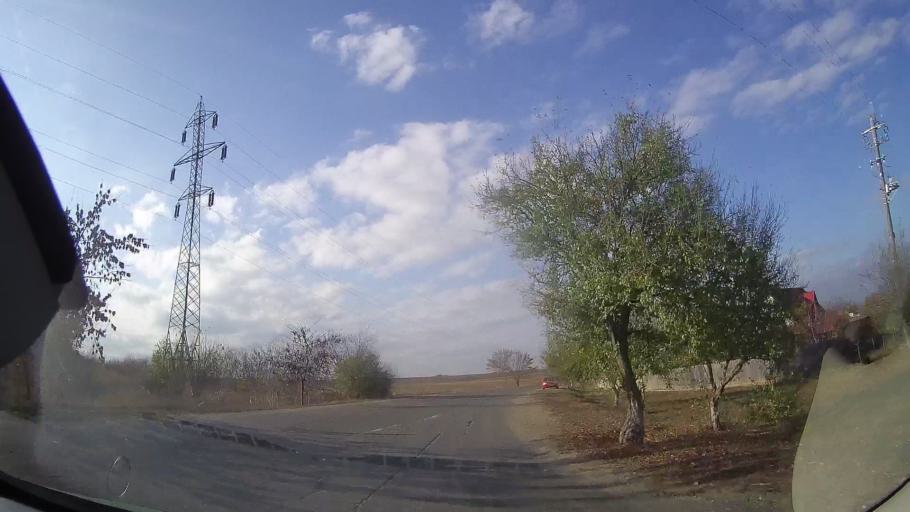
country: RO
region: Constanta
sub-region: Comuna Limanu
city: Limanu
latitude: 43.7945
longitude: 28.5219
